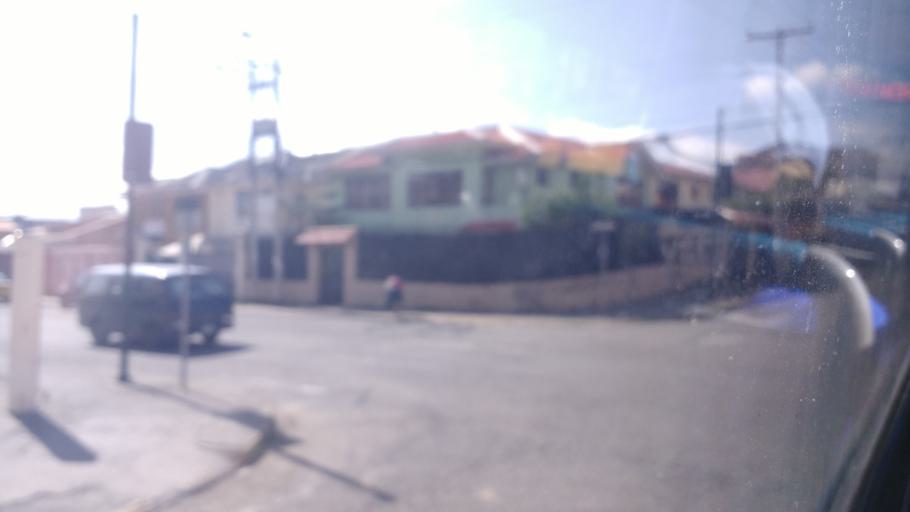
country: EC
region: Azuay
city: Cuenca
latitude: -2.8958
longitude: -79.0234
